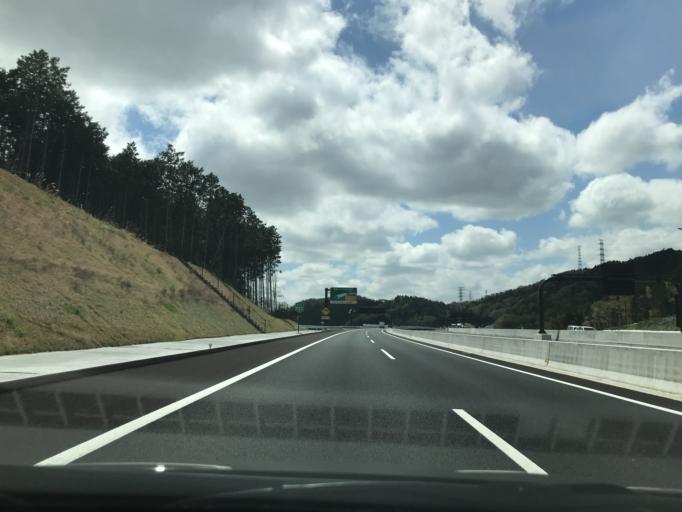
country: JP
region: Osaka
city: Ibaraki
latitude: 34.8766
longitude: 135.5255
